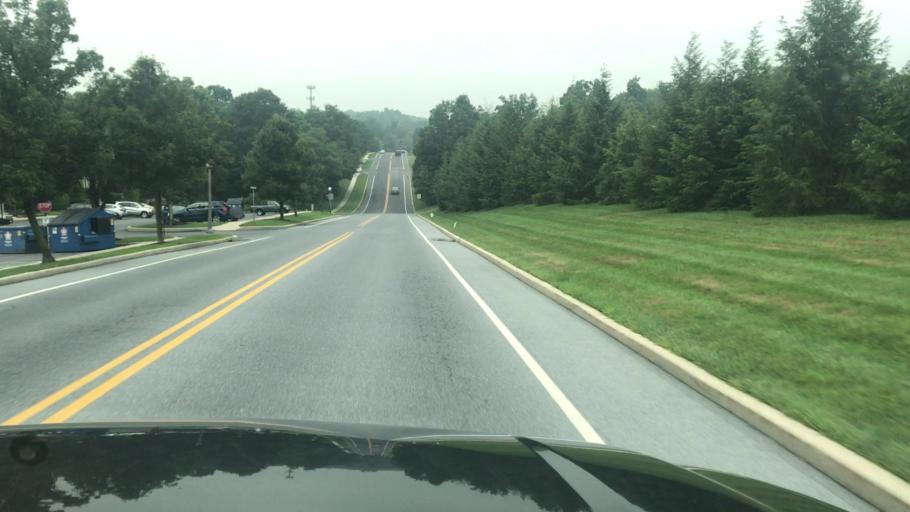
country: US
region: Pennsylvania
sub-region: Cumberland County
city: Enola
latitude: 40.2778
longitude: -76.9727
